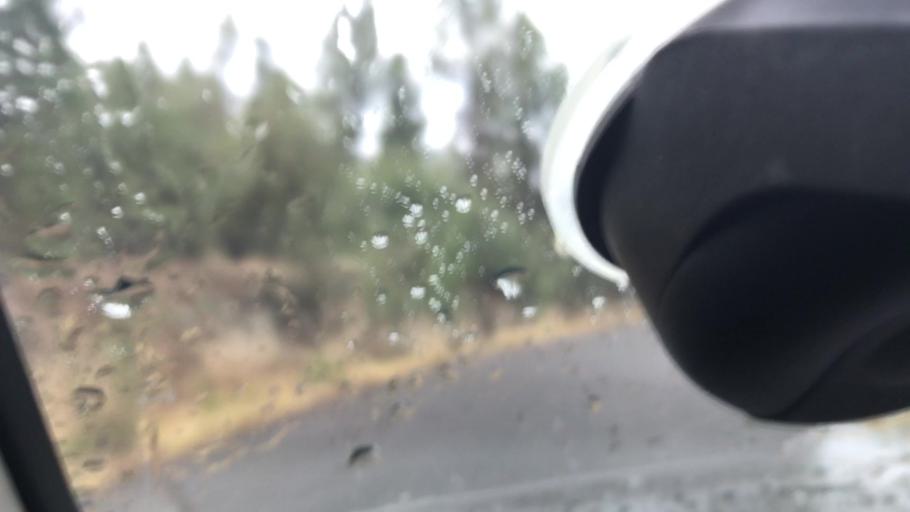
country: US
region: Arizona
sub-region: Yavapai County
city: Prescott
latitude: 34.5096
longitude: -112.3791
